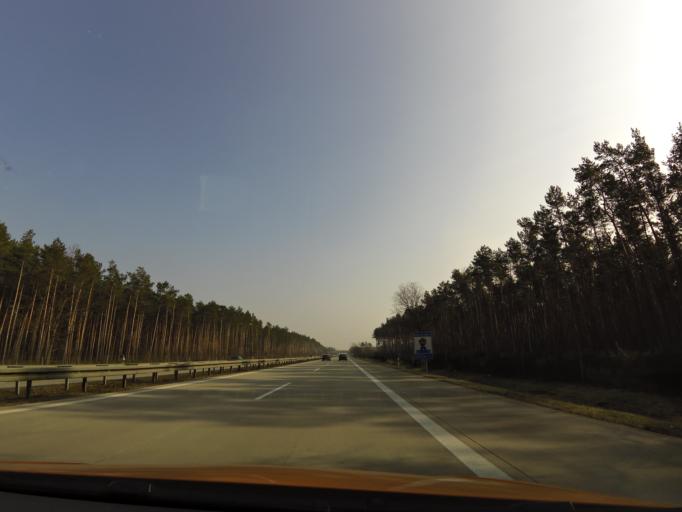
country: DE
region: Brandenburg
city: Briesen
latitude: 52.3237
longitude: 14.3017
